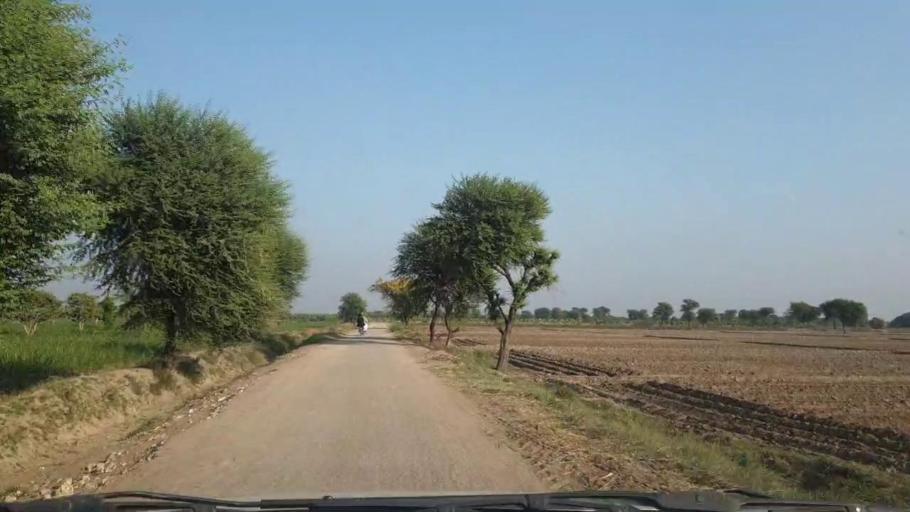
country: PK
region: Sindh
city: Chambar
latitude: 25.2160
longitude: 68.6837
